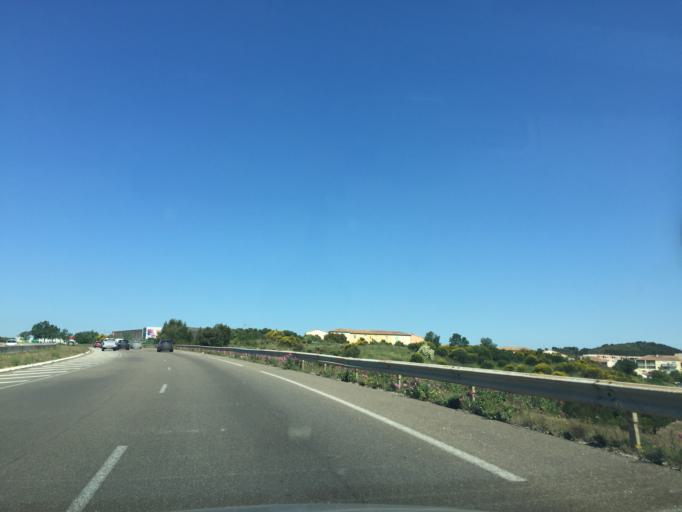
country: FR
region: Languedoc-Roussillon
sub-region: Departement du Gard
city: Les Angles
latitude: 43.9570
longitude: 4.7541
